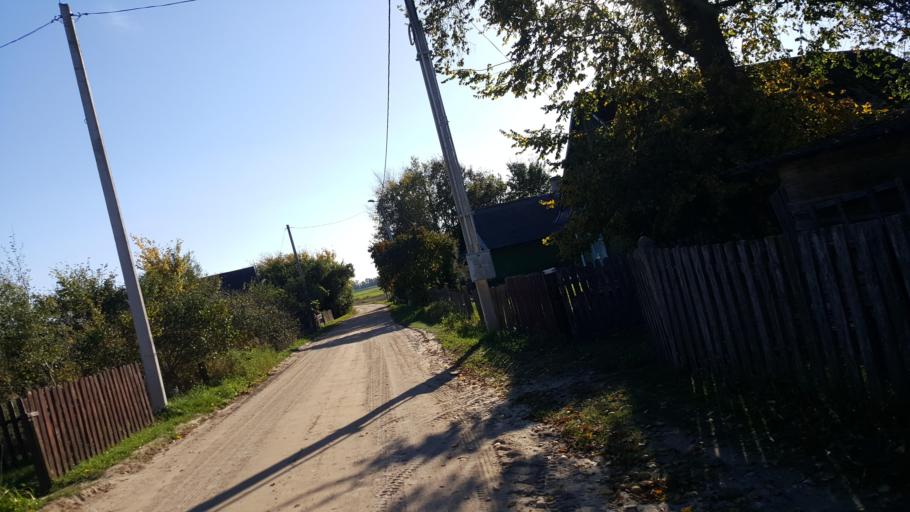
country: BY
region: Brest
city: Kamyanyets
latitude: 52.3875
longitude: 23.8849
